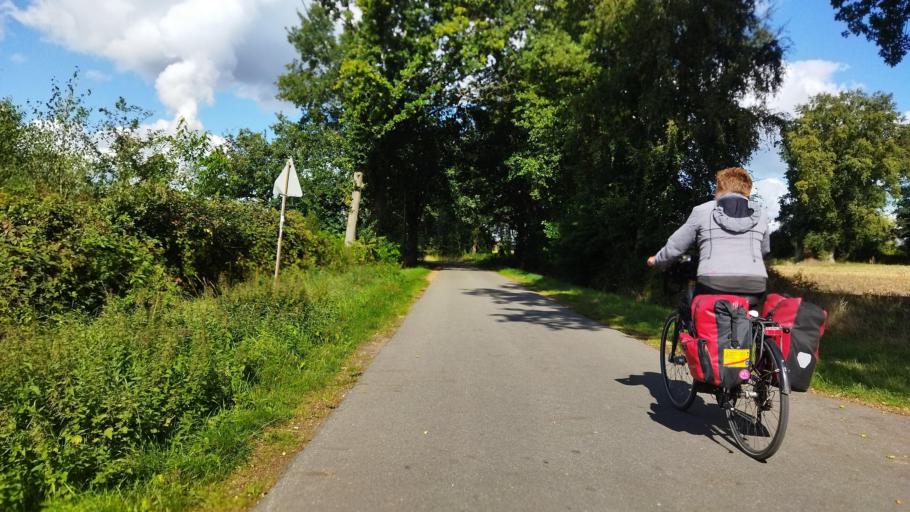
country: DE
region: Lower Saxony
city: Emsburen
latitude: 52.4393
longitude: 7.3398
